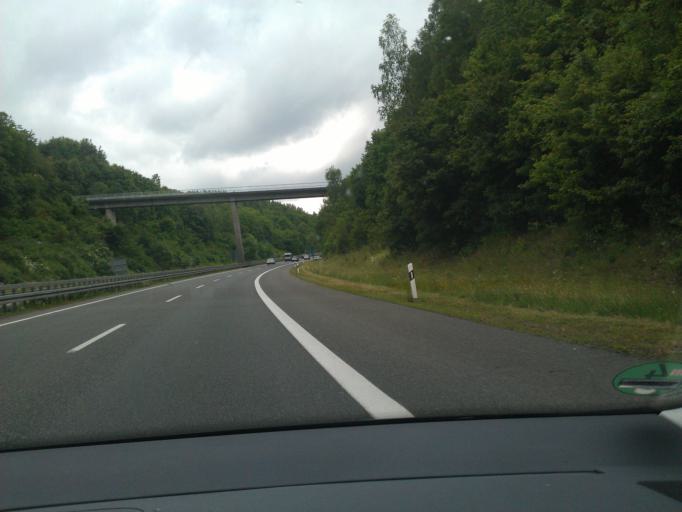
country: DE
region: Saarland
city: Nonnweiler
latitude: 49.6016
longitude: 6.9645
